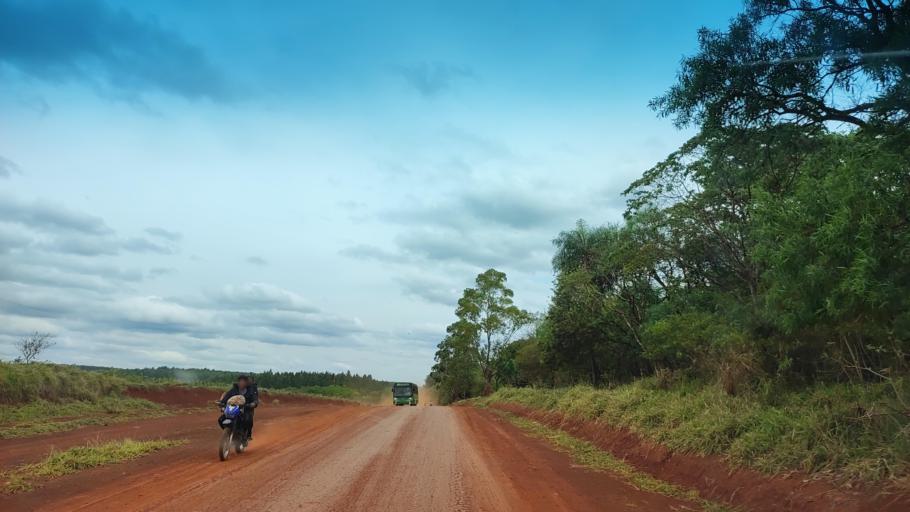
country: AR
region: Misiones
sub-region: Departamento de Capital
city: Posadas
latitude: -27.4860
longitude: -55.9708
